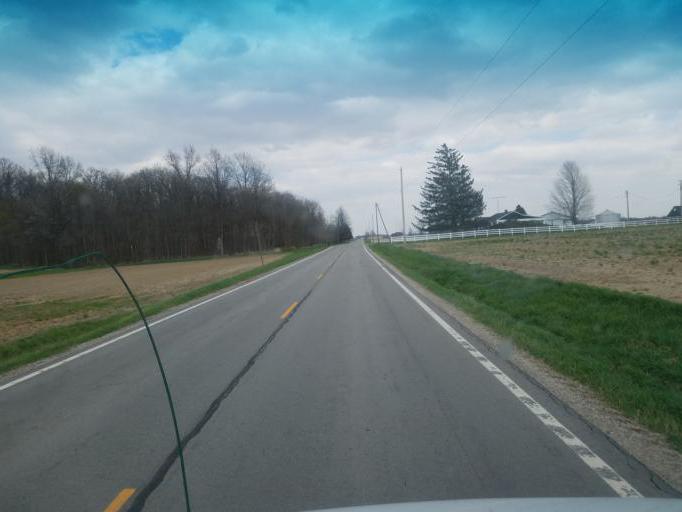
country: US
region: Ohio
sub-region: Crawford County
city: Bucyrus
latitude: 40.9504
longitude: -83.0273
